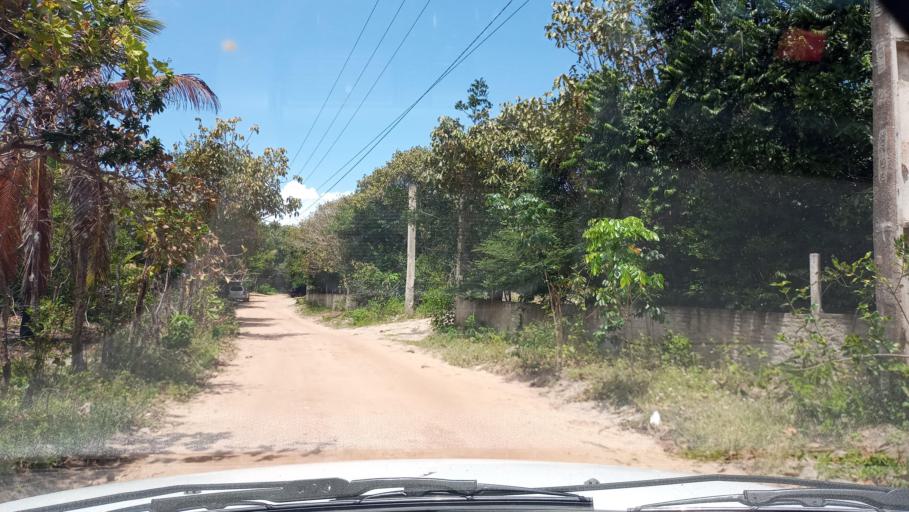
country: BR
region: Rio Grande do Norte
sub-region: Ares
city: Ares
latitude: -6.2425
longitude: -35.0441
